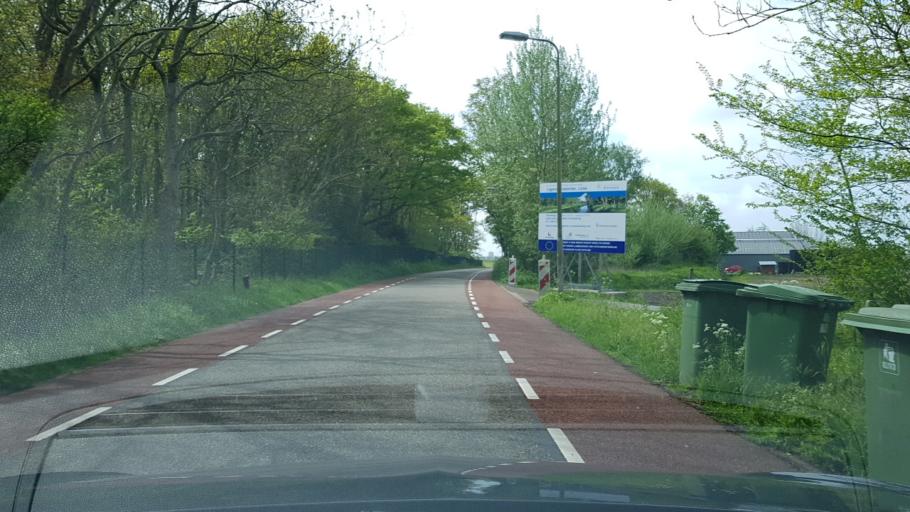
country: NL
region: South Holland
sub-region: Gemeente Teylingen
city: Sassenheim
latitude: 52.2537
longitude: 4.5268
